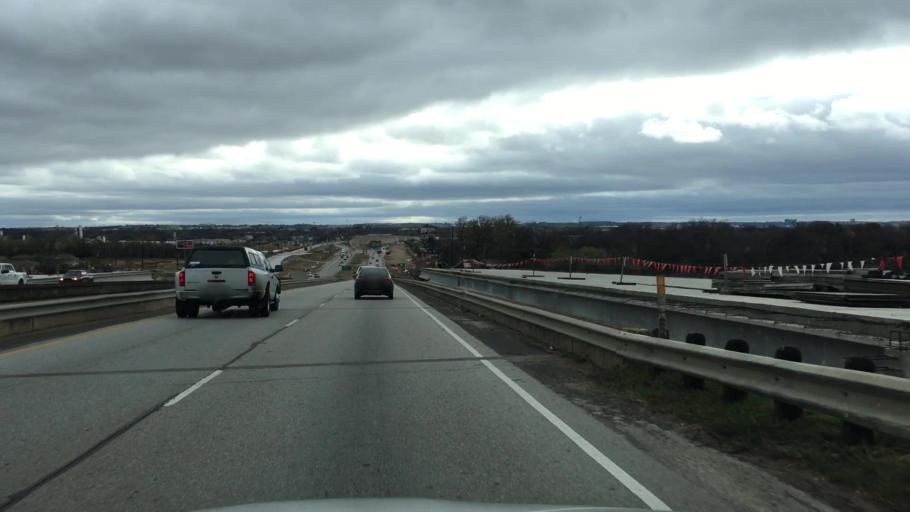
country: US
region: Texas
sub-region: Travis County
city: Austin
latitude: 30.2642
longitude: -97.6724
